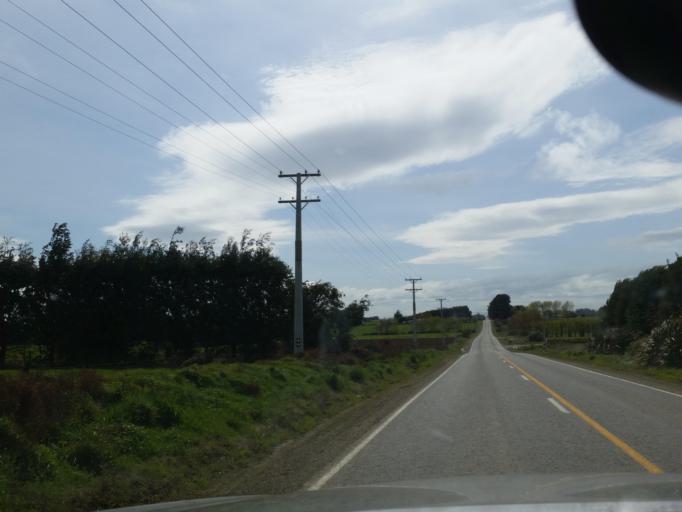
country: NZ
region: Southland
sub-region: Invercargill City
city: Invercargill
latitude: -46.3699
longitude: 168.4536
